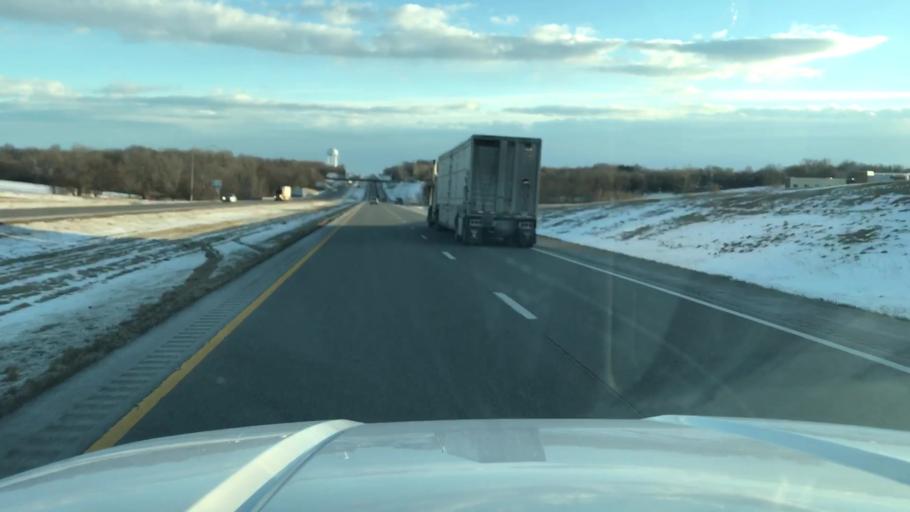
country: US
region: Missouri
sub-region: Andrew County
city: Country Club Village
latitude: 39.8133
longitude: -94.8033
